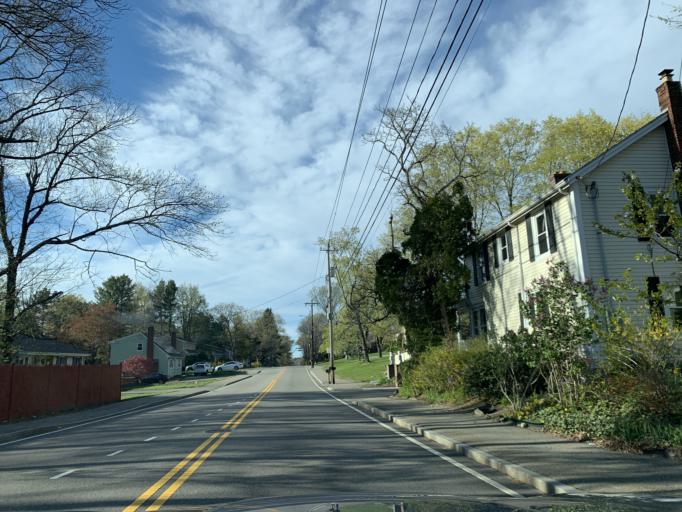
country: US
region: Massachusetts
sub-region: Norfolk County
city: Stoughton
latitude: 42.1280
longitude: -71.0750
